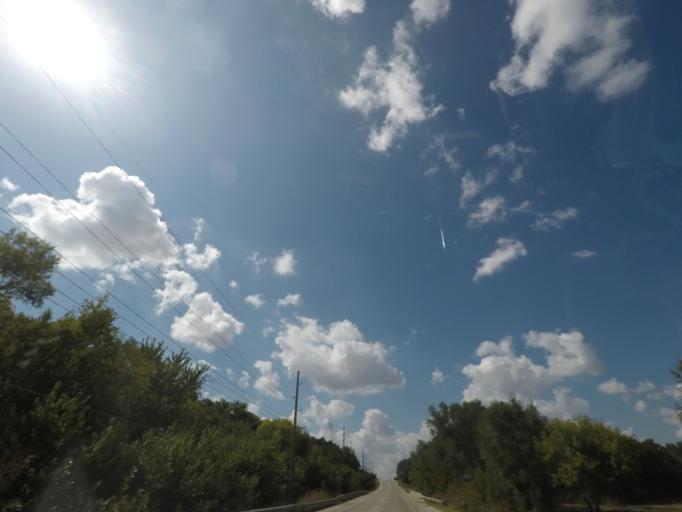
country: US
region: Iowa
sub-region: Story County
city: Nevada
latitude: 42.0228
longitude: -93.4671
